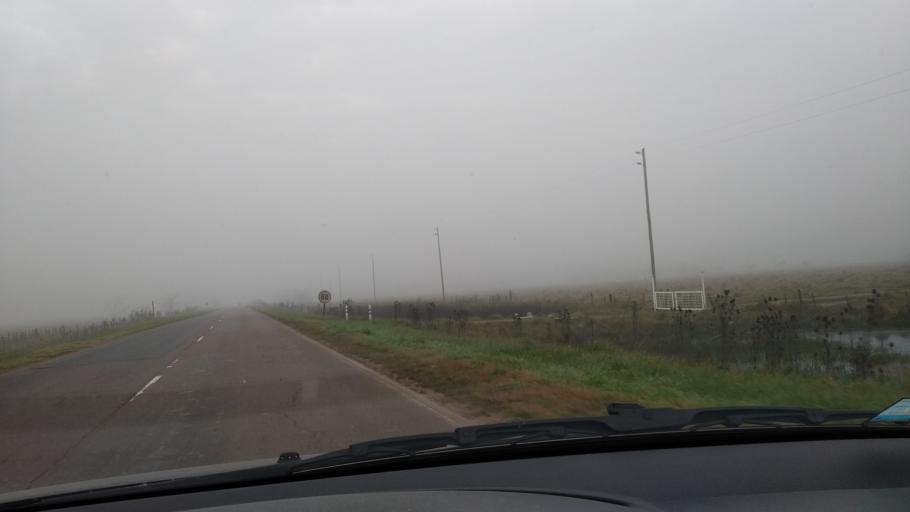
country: AR
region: Buenos Aires
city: San Miguel del Monte
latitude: -35.3055
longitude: -58.5945
